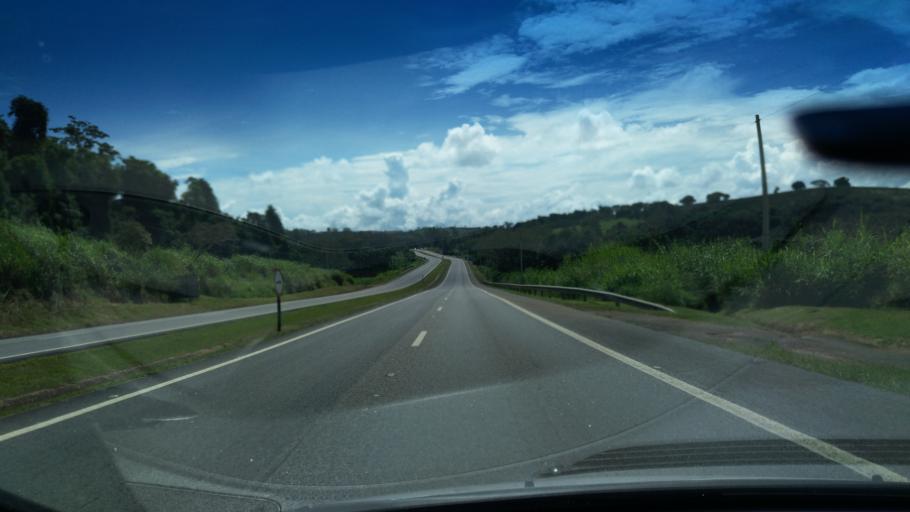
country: BR
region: Sao Paulo
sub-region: Santo Antonio Do Jardim
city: Espirito Santo do Pinhal
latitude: -22.2343
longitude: -46.7976
